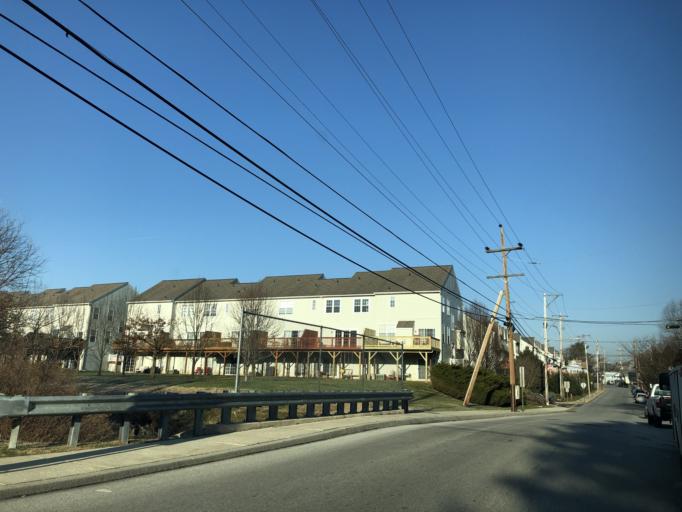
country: US
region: Pennsylvania
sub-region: Chester County
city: Downingtown
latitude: 40.0052
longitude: -75.6980
